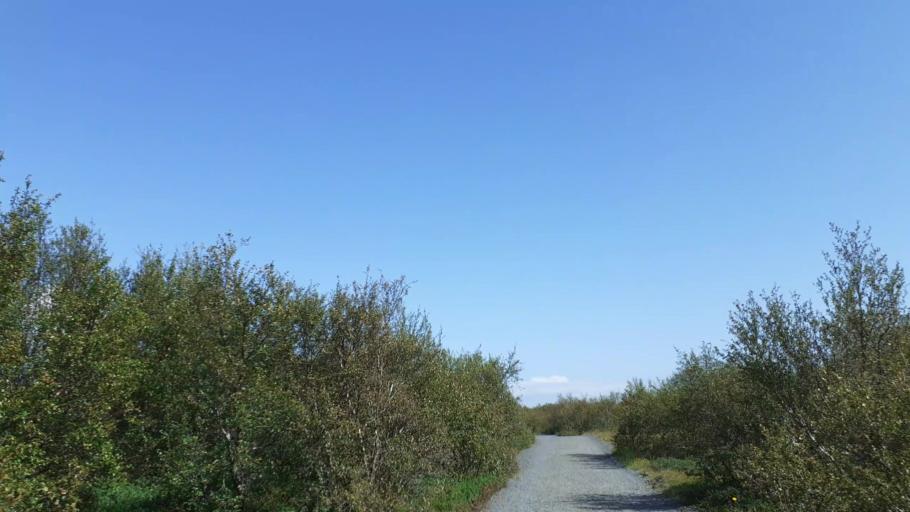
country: IS
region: West
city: Borgarnes
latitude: 64.7524
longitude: -21.5521
